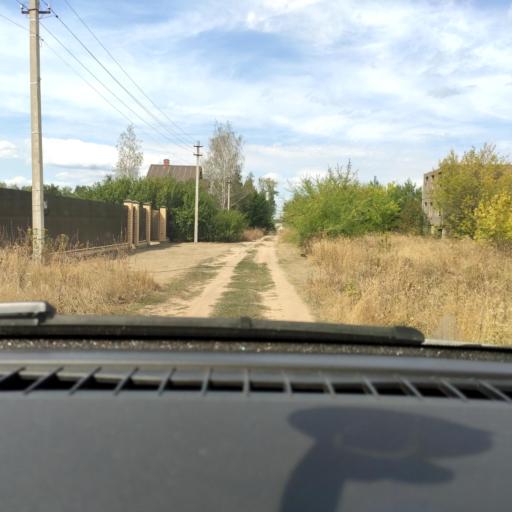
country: RU
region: Voronezj
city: Novaya Usman'
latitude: 51.6669
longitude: 39.4401
